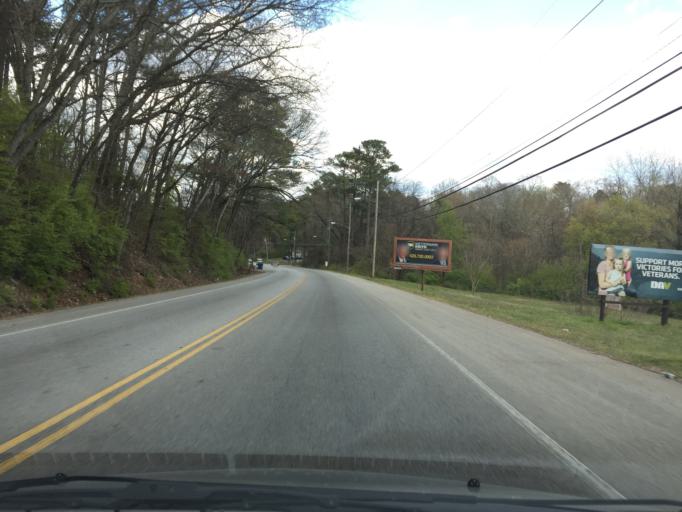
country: US
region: Tennessee
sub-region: Hamilton County
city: East Chattanooga
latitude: 35.0746
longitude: -85.2331
